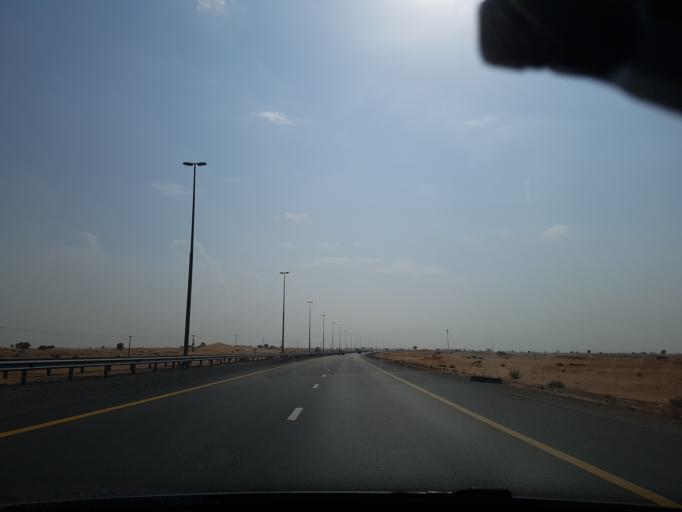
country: AE
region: Umm al Qaywayn
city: Umm al Qaywayn
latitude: 25.5423
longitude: 55.7780
